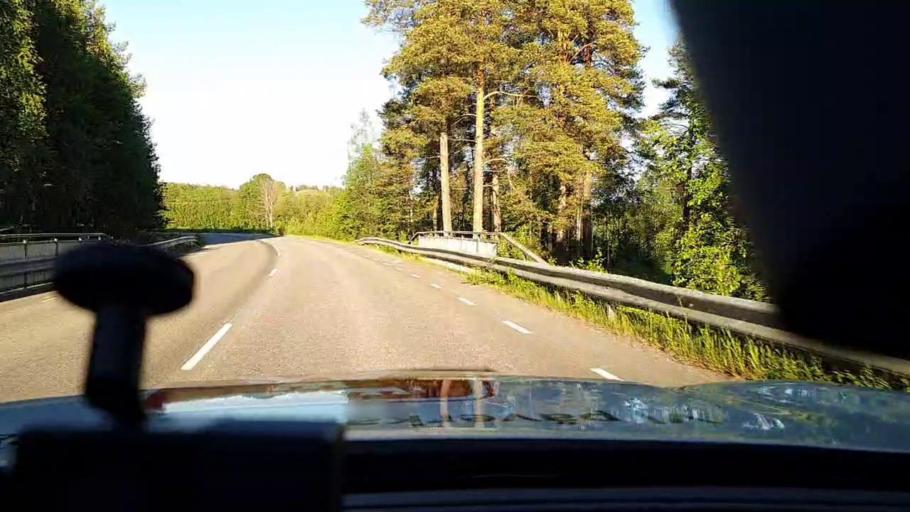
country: SE
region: Norrbotten
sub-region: Lulea Kommun
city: Lulea
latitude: 65.6074
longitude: 22.1712
